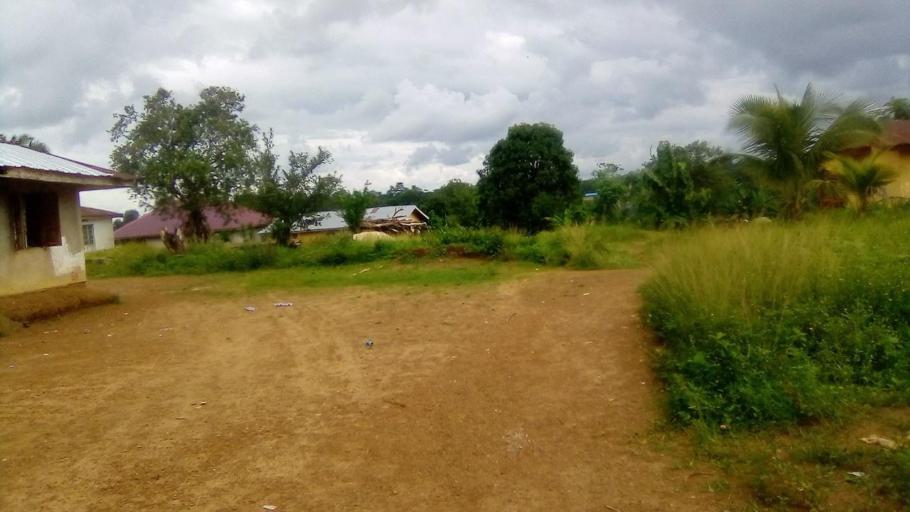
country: SL
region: Southern Province
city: Pujehun
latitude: 7.3609
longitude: -11.7243
